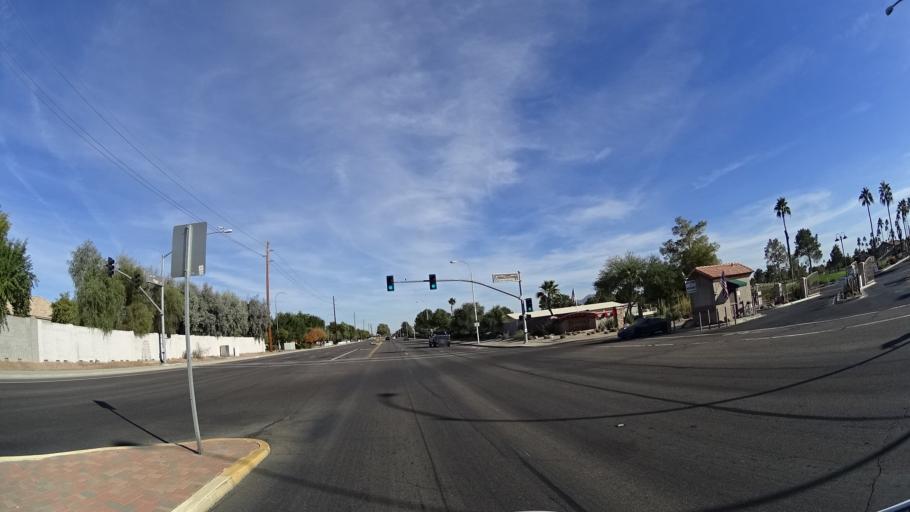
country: US
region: Arizona
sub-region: Maricopa County
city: Sun Lakes
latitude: 33.2189
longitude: -111.8135
